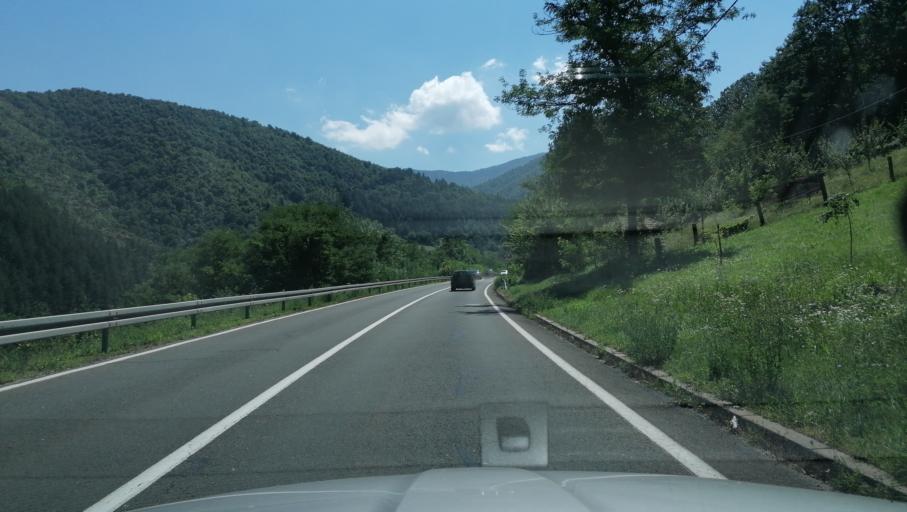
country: RS
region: Central Serbia
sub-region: Raski Okrug
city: Kraljevo
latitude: 43.6644
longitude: 20.5917
